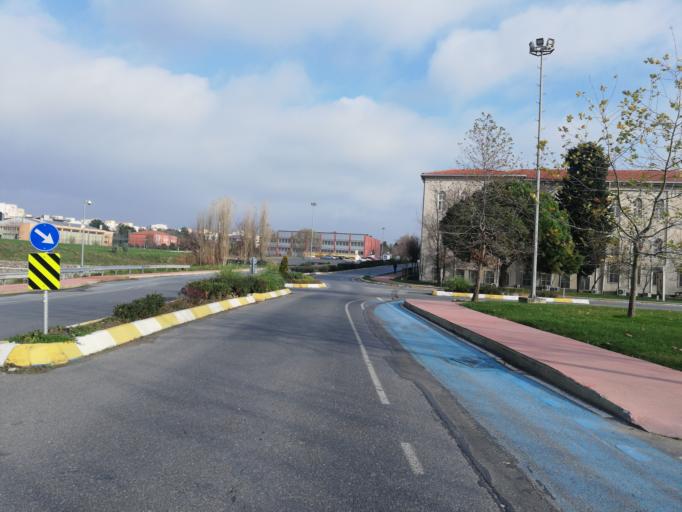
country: TR
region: Istanbul
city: merter keresteciler
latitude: 41.0247
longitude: 28.8868
